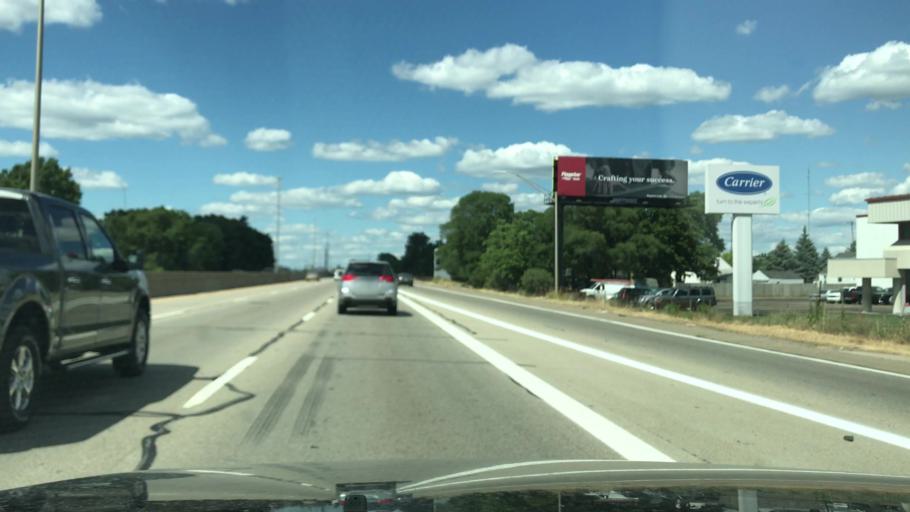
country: US
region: Michigan
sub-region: Kent County
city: Wyoming
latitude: 42.8867
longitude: -85.6798
